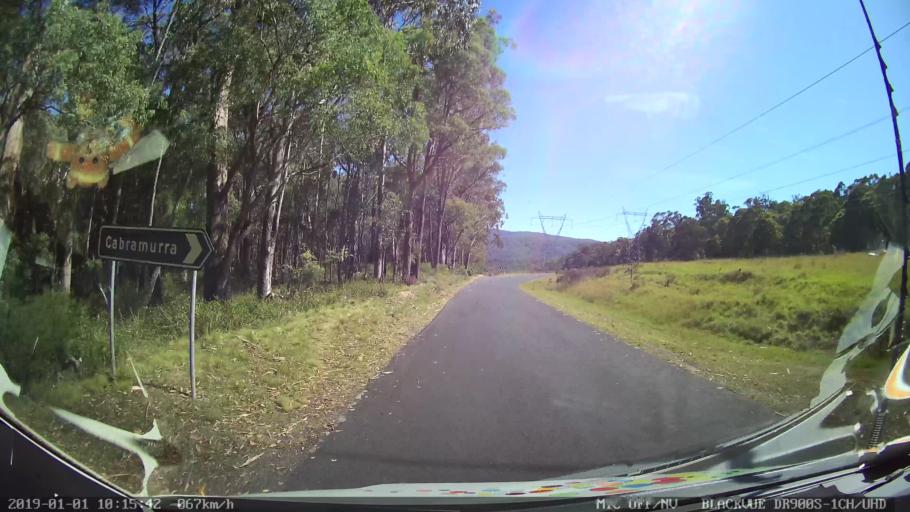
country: AU
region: New South Wales
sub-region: Snowy River
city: Jindabyne
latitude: -36.0991
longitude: 148.1621
